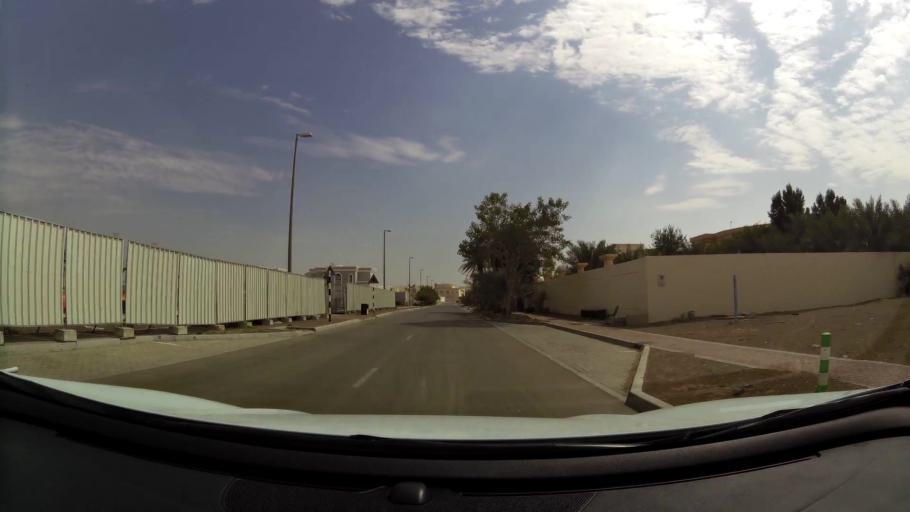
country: AE
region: Abu Dhabi
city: Al Ain
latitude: 24.1972
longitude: 55.8089
